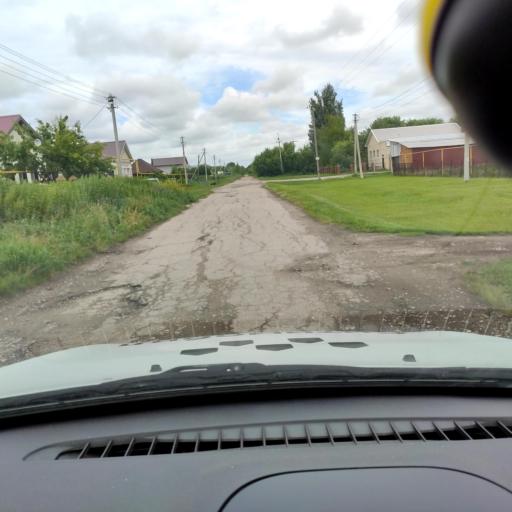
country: RU
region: Samara
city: Tol'yatti
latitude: 53.6484
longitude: 49.3008
